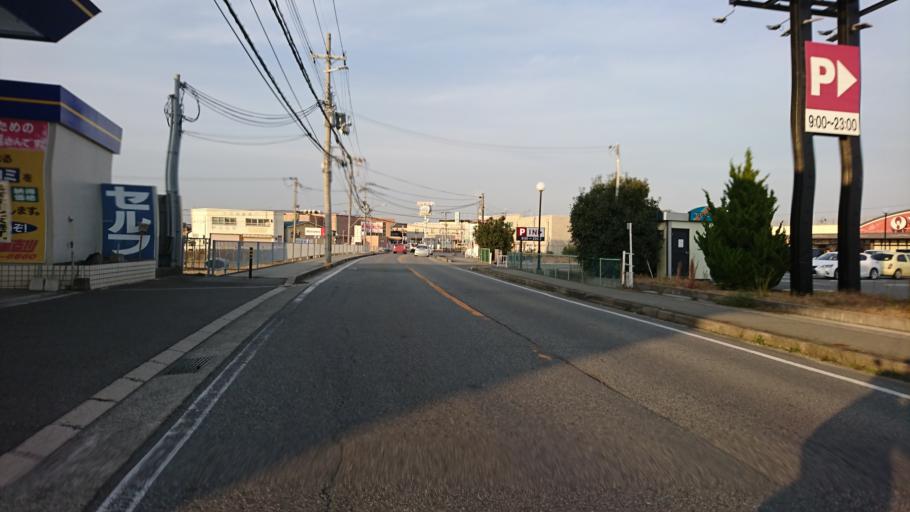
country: JP
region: Hyogo
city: Kakogawacho-honmachi
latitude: 34.7570
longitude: 134.8736
